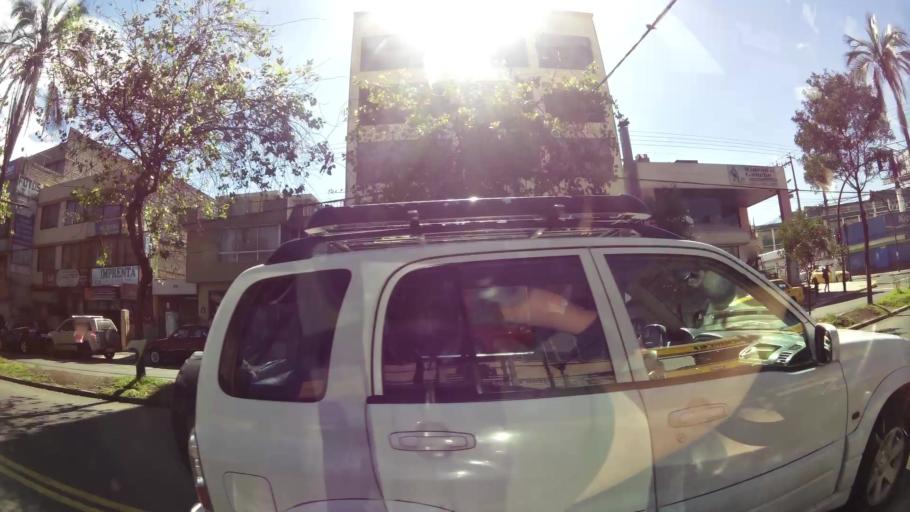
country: EC
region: Pichincha
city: Quito
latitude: -0.2431
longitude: -78.5201
